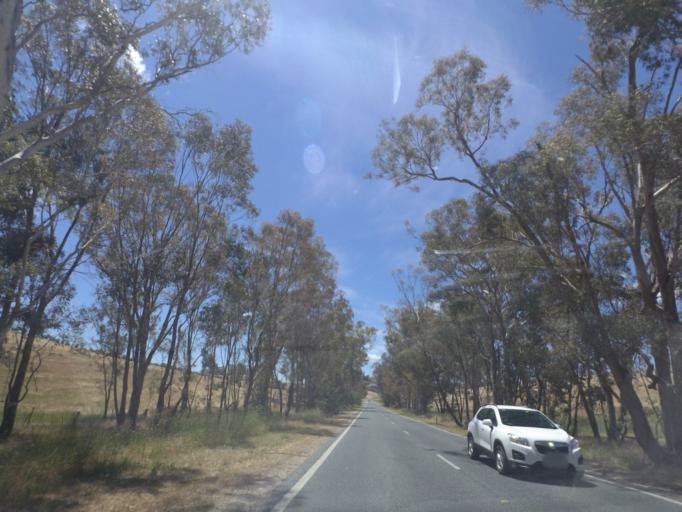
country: AU
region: Victoria
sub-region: Mount Alexander
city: Castlemaine
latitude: -37.1958
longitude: 144.1474
